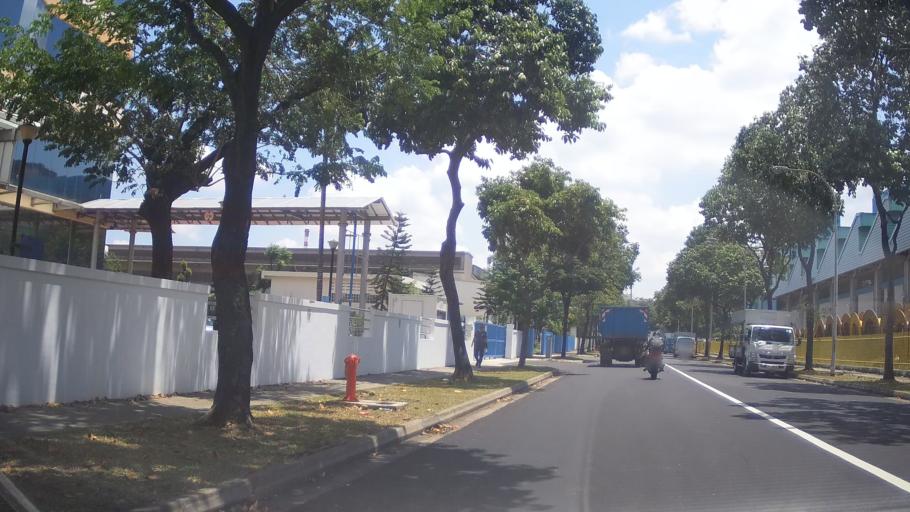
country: SG
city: Singapore
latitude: 1.3053
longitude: 103.6745
